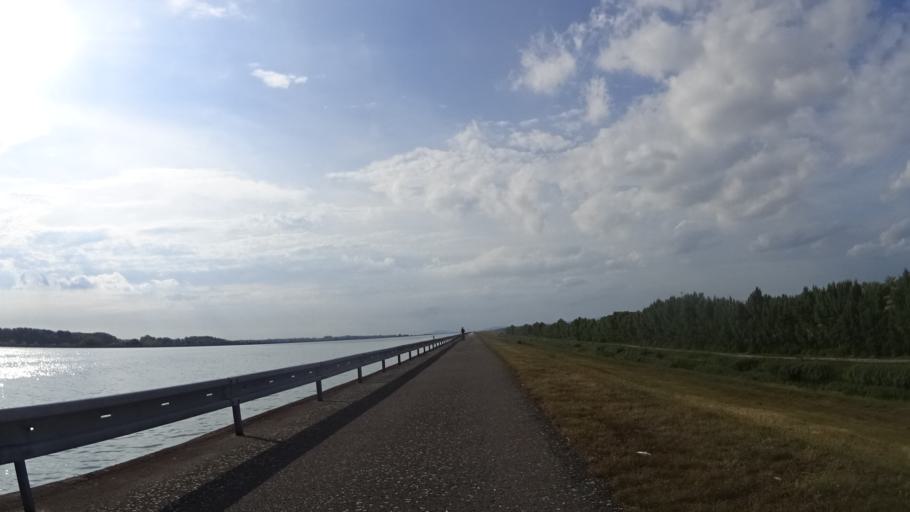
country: HU
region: Gyor-Moson-Sopron
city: Asvanyraro
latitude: 47.9399
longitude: 17.4555
